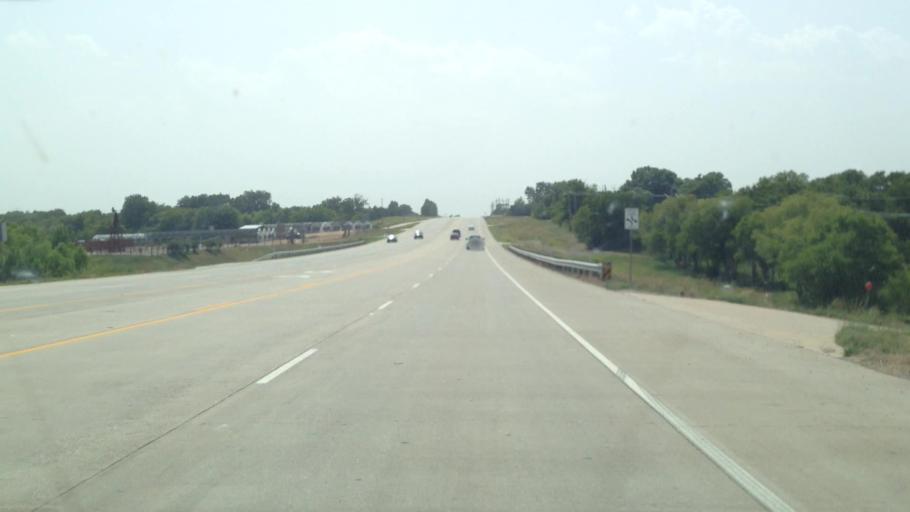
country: US
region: Texas
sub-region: Collin County
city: Farmersville
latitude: 33.1592
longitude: -96.3976
